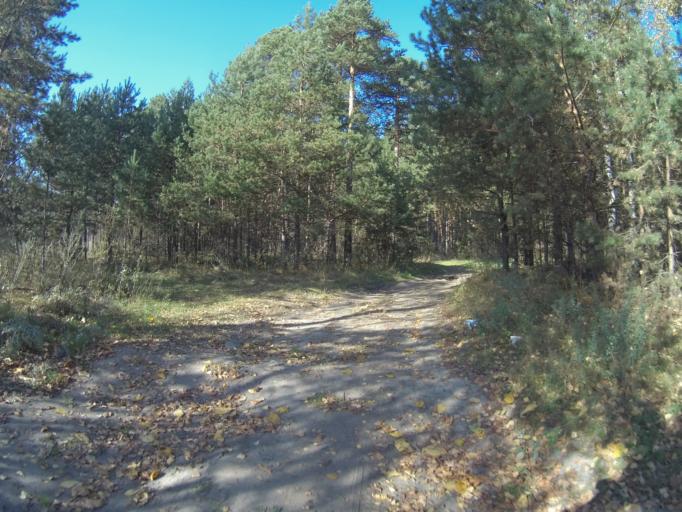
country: RU
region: Vladimir
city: Raduzhnyy
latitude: 56.0228
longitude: 40.3856
